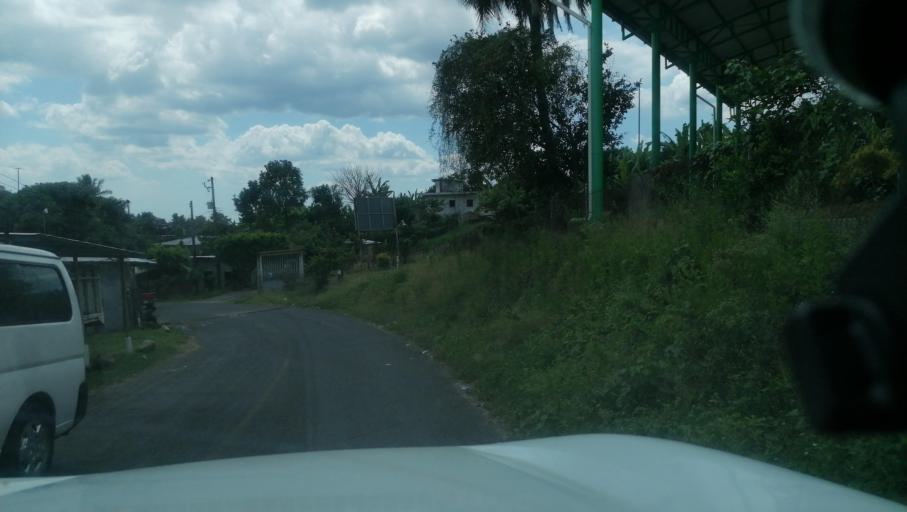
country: MX
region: Chiapas
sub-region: Cacahoatan
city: Benito Juarez
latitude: 15.0475
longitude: -92.1524
